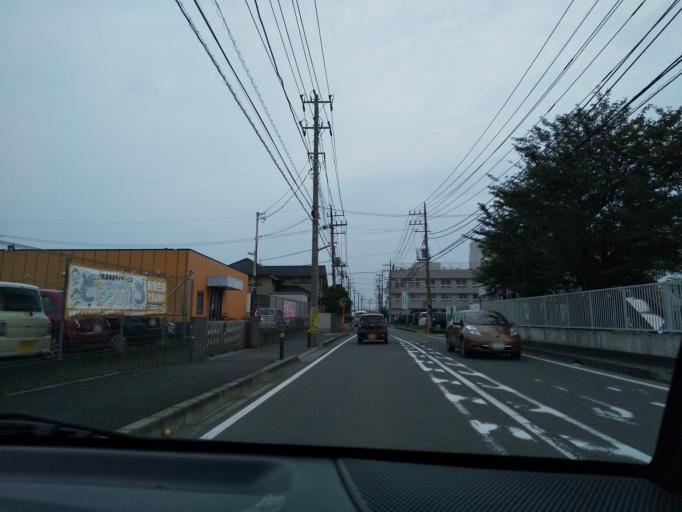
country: JP
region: Kanagawa
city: Atsugi
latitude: 35.4208
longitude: 139.3918
